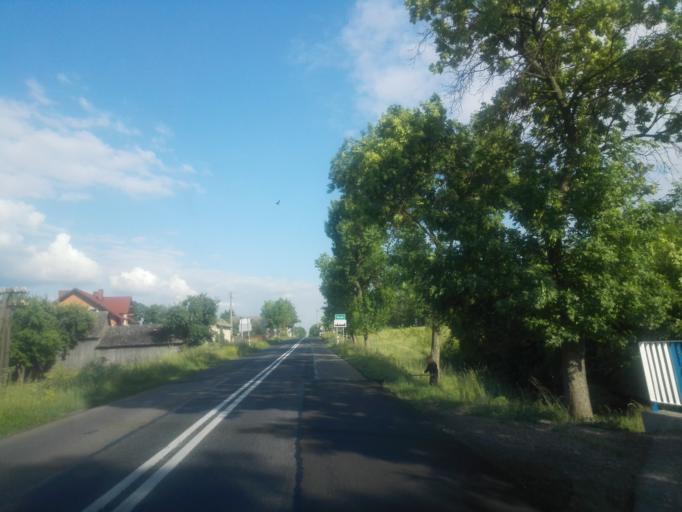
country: PL
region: Silesian Voivodeship
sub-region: Powiat czestochowski
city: Potok Zloty
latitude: 50.7350
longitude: 19.3940
